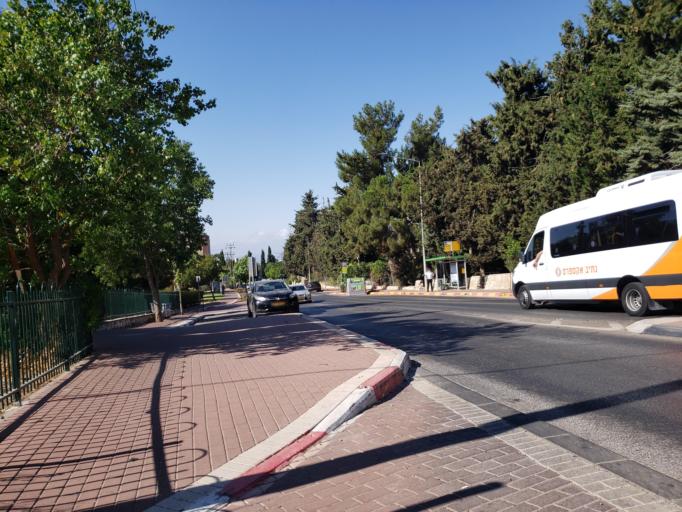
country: IL
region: Northern District
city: Safed
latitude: 32.9614
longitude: 35.4986
